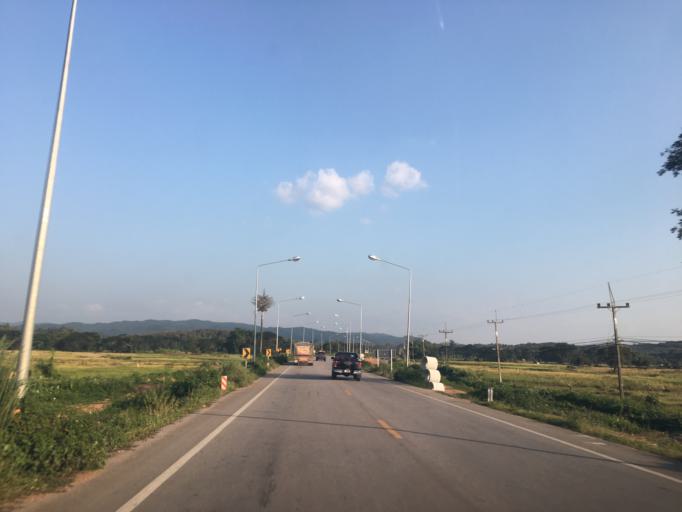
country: TH
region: Lampang
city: Ngao
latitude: 18.7202
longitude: 99.9735
